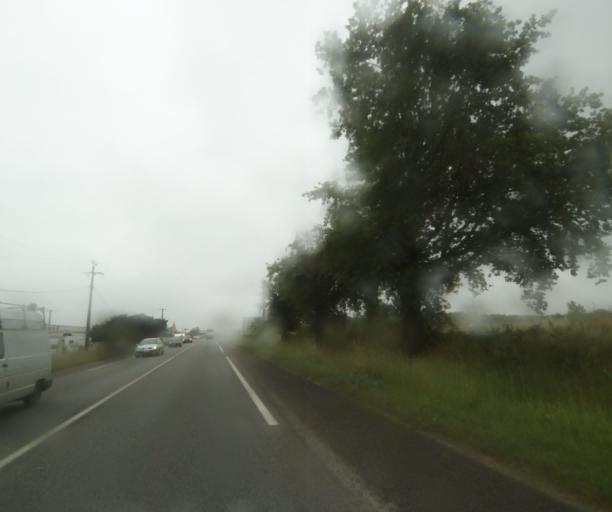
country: FR
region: Midi-Pyrenees
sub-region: Departement du Tarn-et-Garonne
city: Albias
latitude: 44.0578
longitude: 1.4060
